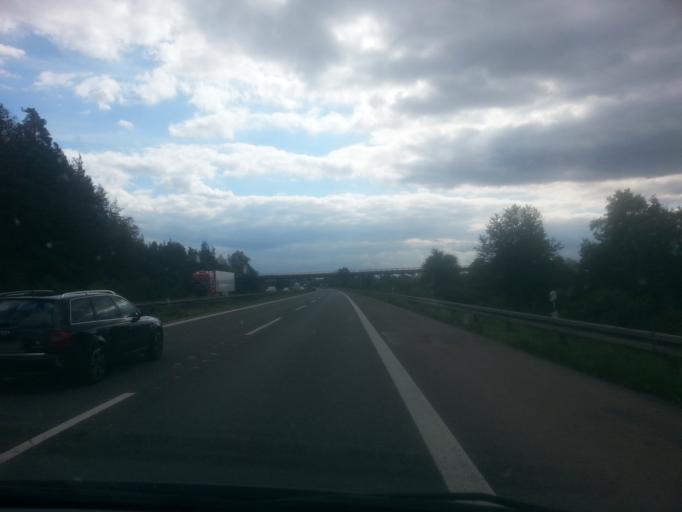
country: DE
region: Bavaria
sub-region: Upper Palatinate
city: Stulln
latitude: 49.4181
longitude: 12.1668
